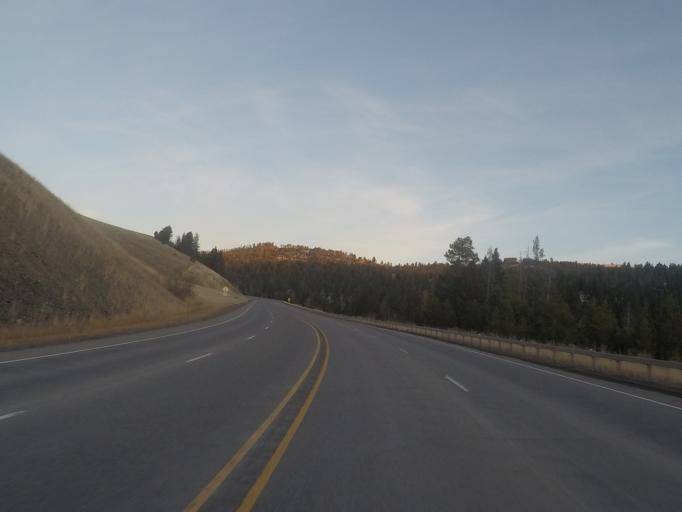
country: US
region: Montana
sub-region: Lewis and Clark County
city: Helena West Side
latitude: 46.5578
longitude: -112.3702
